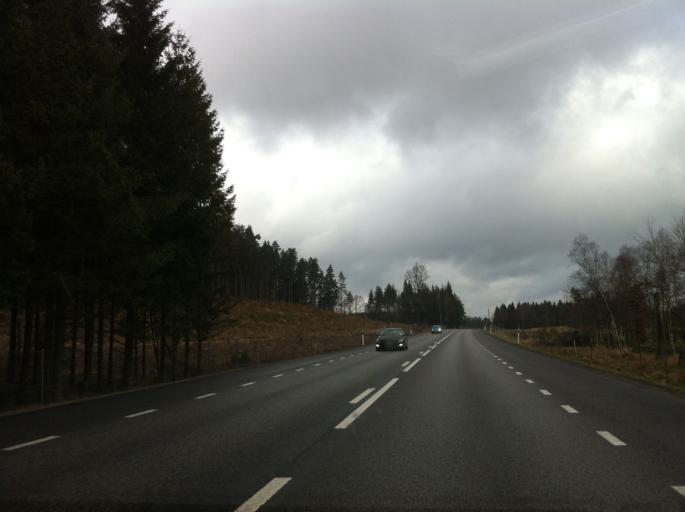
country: SE
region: Halland
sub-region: Halmstads Kommun
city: Aled
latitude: 56.7681
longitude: 12.9487
